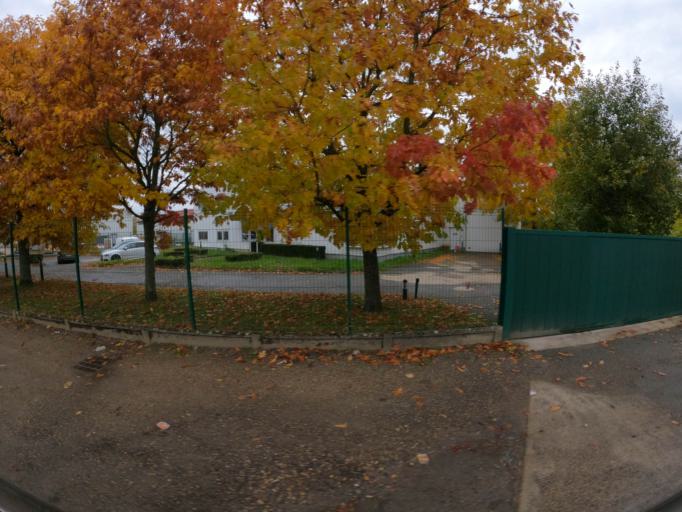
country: FR
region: Ile-de-France
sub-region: Departement de Seine-et-Marne
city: Chanteloup-en-Brie
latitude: 48.8337
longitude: 2.7537
